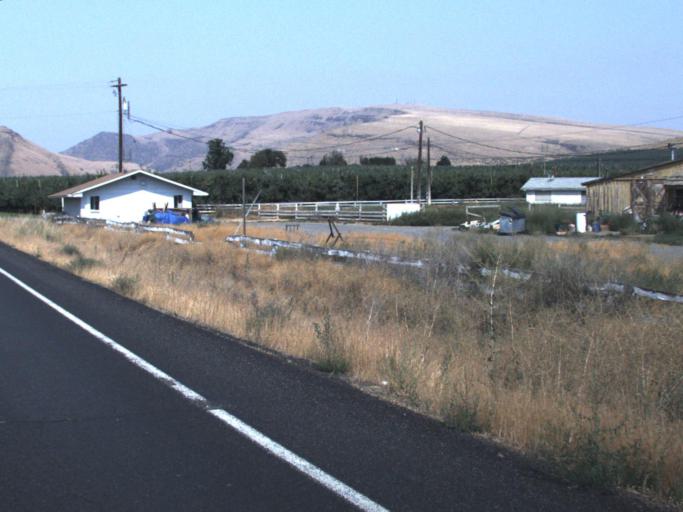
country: US
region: Washington
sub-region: Yakima County
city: Selah
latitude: 46.6931
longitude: -120.4762
